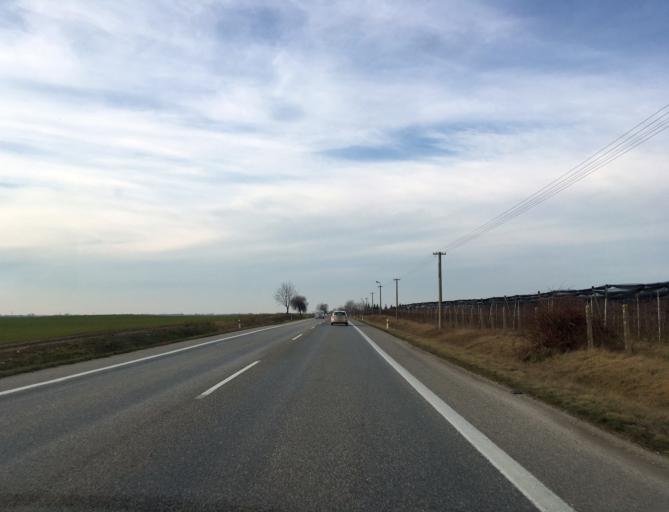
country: SK
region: Nitriansky
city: Surany
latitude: 48.1078
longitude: 18.0516
